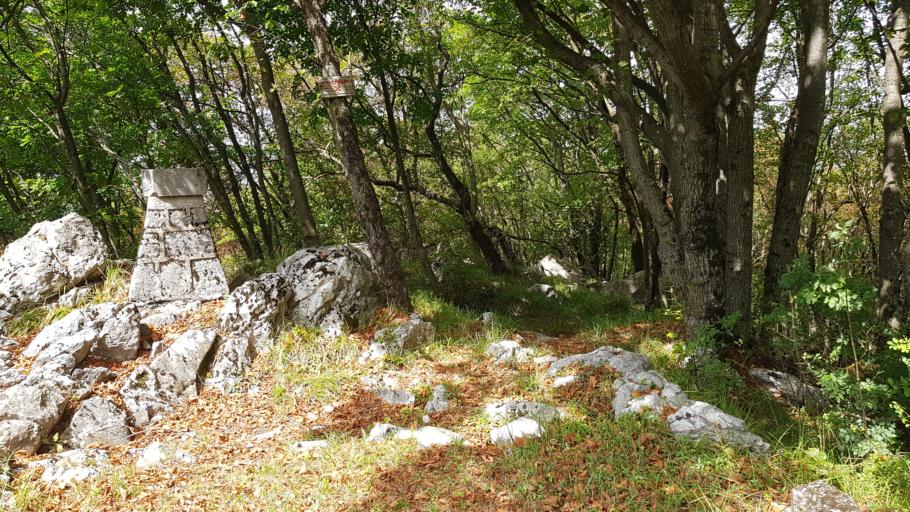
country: SI
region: Kanal
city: Deskle
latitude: 46.0158
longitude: 13.6334
